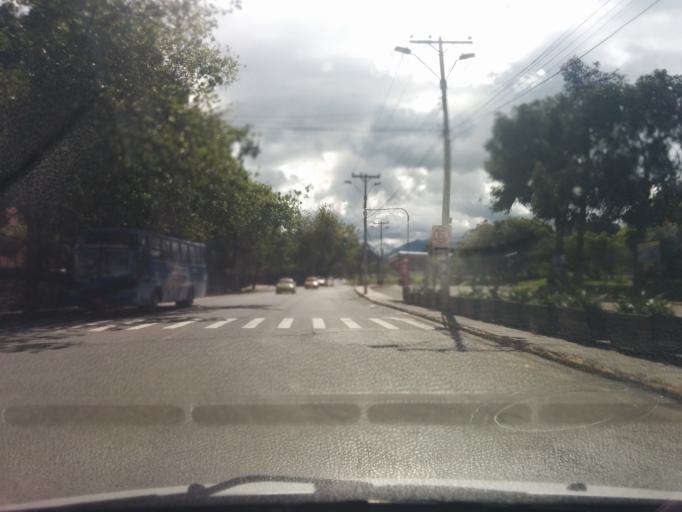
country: EC
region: Azuay
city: Cuenca
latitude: -2.9178
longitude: -78.9994
